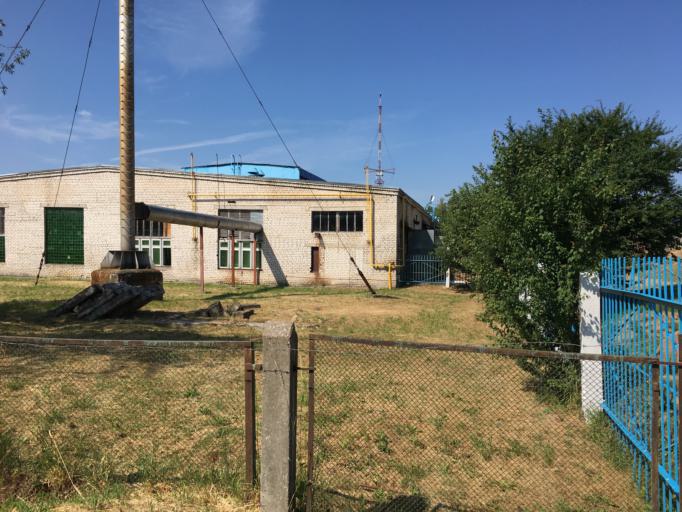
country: BY
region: Grodnenskaya
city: Hrodna
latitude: 53.7039
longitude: 23.8359
